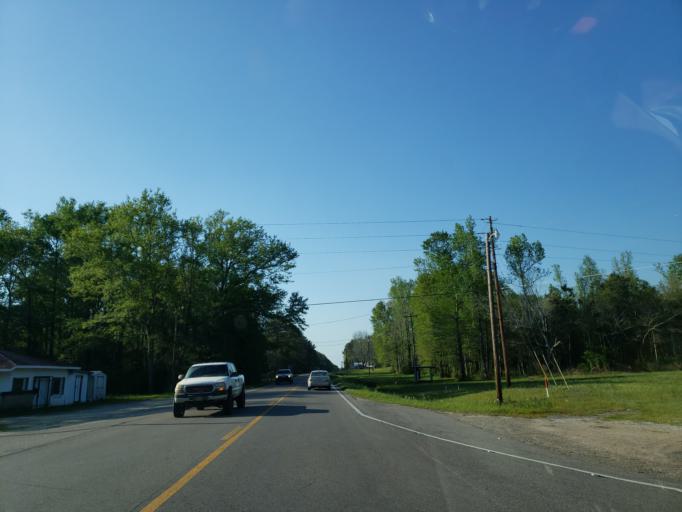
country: US
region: Mississippi
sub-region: Jones County
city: Laurel
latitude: 31.6272
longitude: -89.0901
